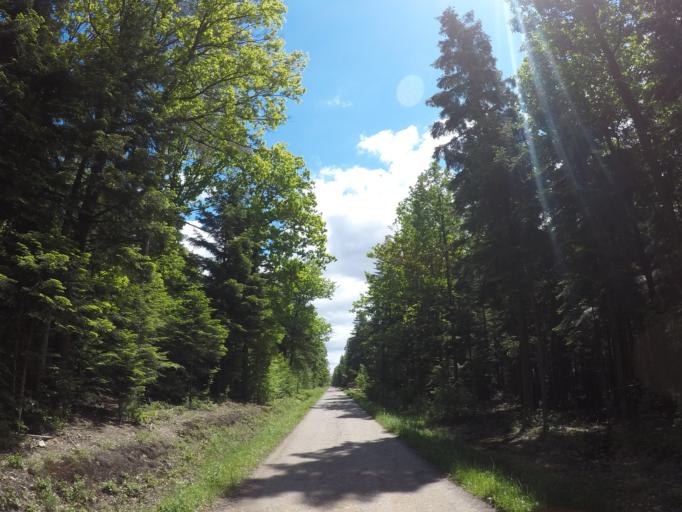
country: PL
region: Swietokrzyskie
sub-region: Powiat kielecki
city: Kielce
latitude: 50.9141
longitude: 20.6506
